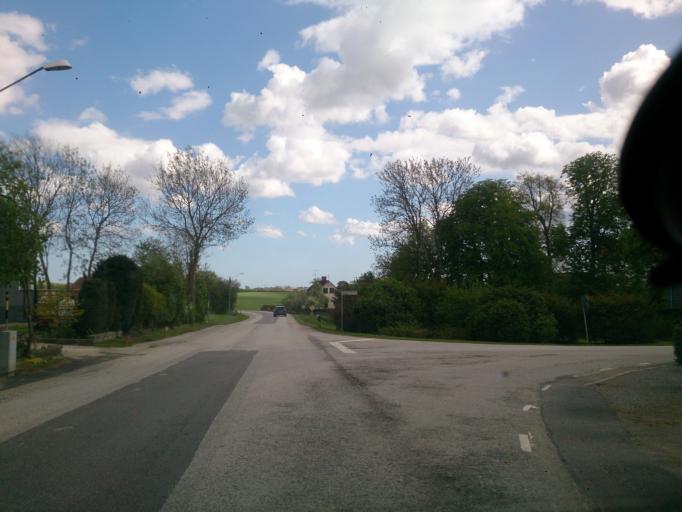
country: SE
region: Skane
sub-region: Ystads Kommun
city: Ystad
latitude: 55.4875
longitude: 13.7133
